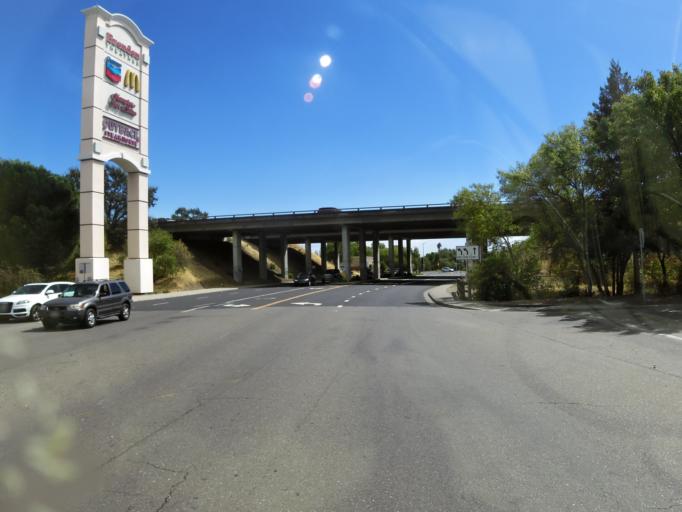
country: US
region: California
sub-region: Solano County
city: Vacaville
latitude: 38.3516
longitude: -121.9861
